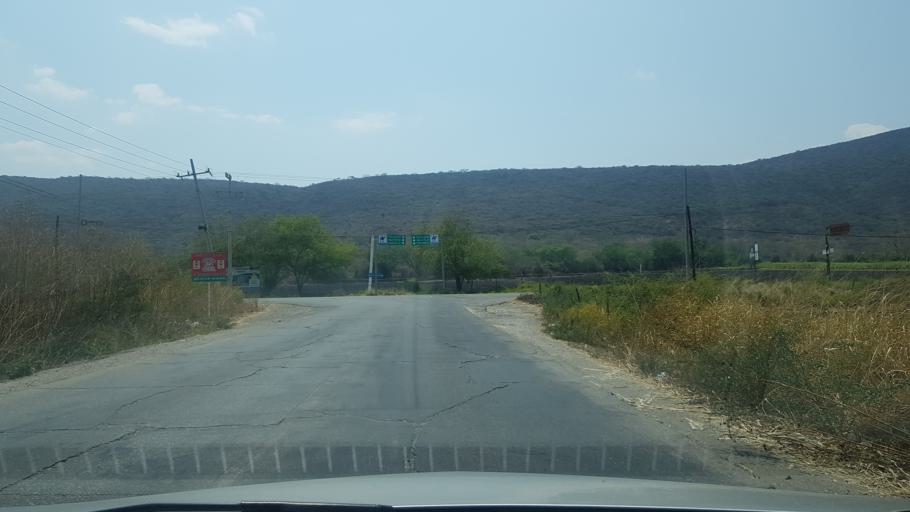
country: MX
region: Morelos
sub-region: Tlaltizapan de Zapata
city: Colonia Palo Prieto (Chipitongo)
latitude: 18.7293
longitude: -99.1236
